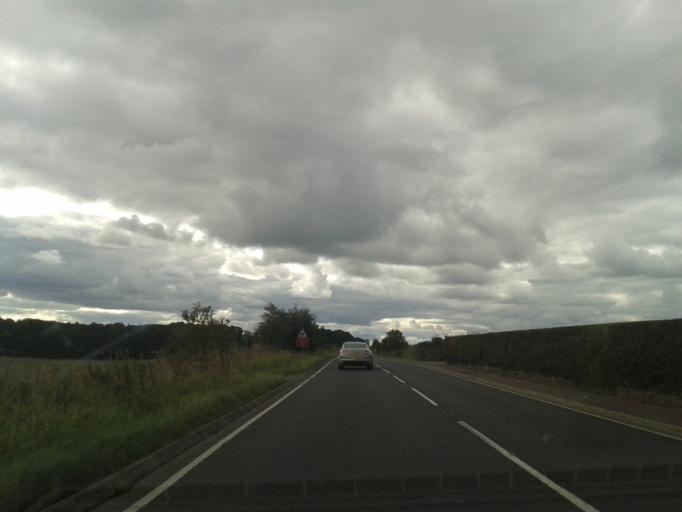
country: GB
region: Scotland
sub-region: Fife
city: Ceres
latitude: 56.3359
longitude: -2.9695
